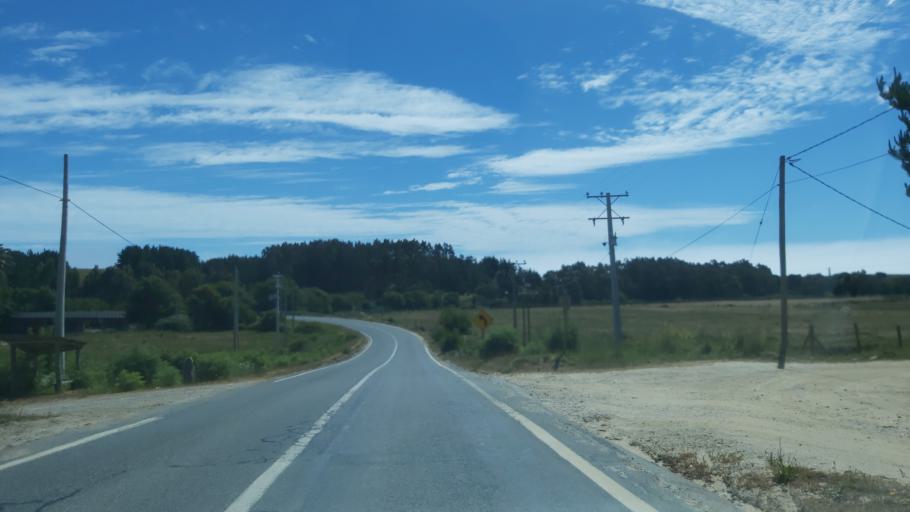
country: CL
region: Maule
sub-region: Provincia de Talca
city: Constitucion
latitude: -35.5660
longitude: -72.6004
